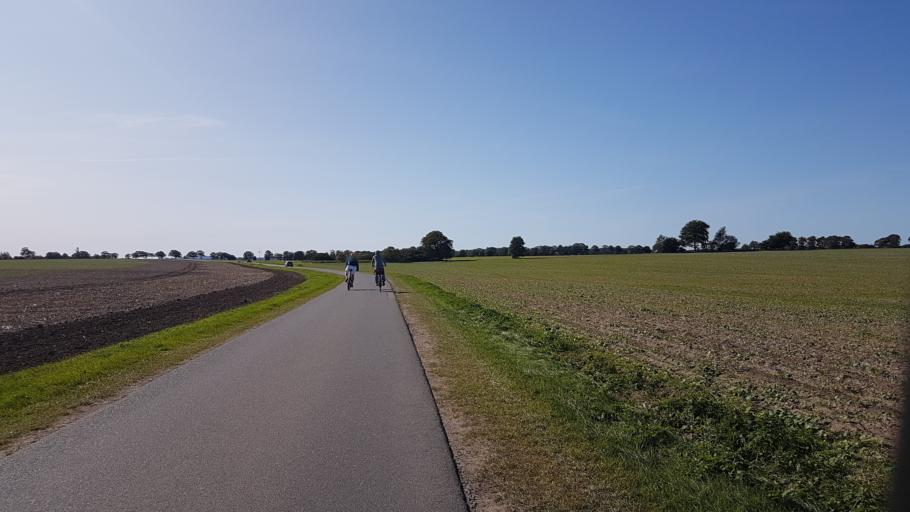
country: DE
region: Mecklenburg-Vorpommern
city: Altenkirchen
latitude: 54.6720
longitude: 13.3760
